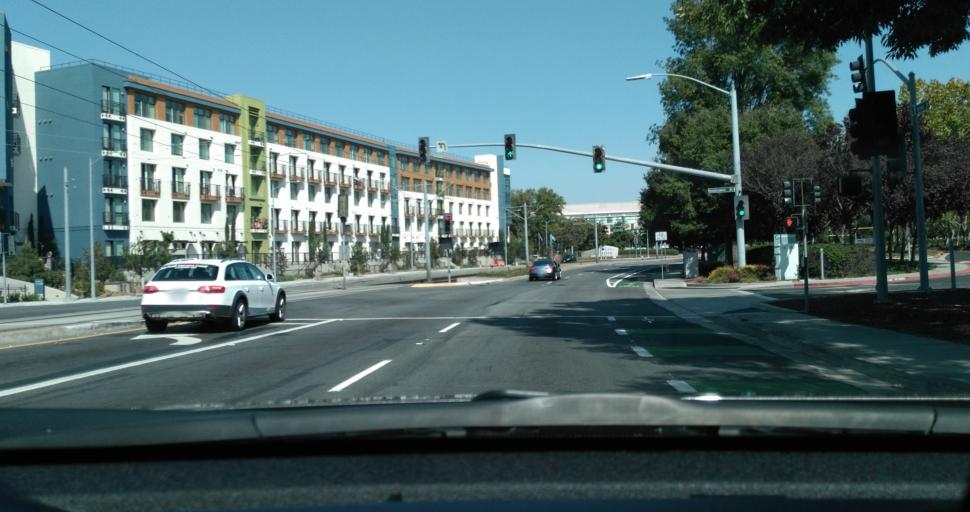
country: US
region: California
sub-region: Santa Clara County
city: Milpitas
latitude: 37.4111
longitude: -121.9585
